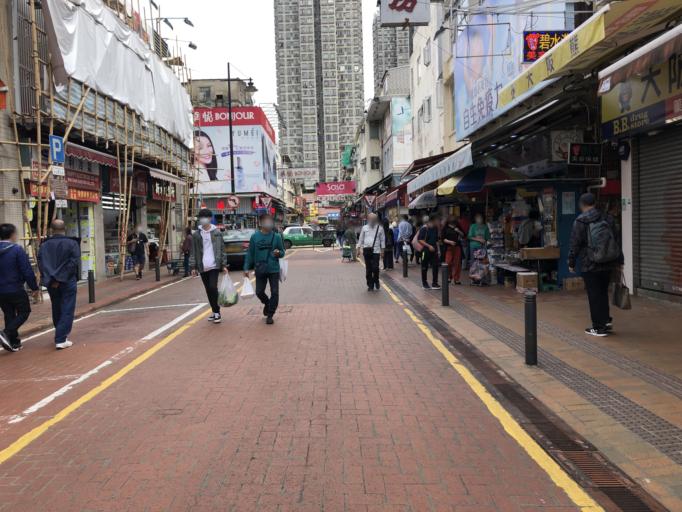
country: HK
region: Tai Po
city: Tai Po
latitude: 22.5044
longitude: 114.1285
